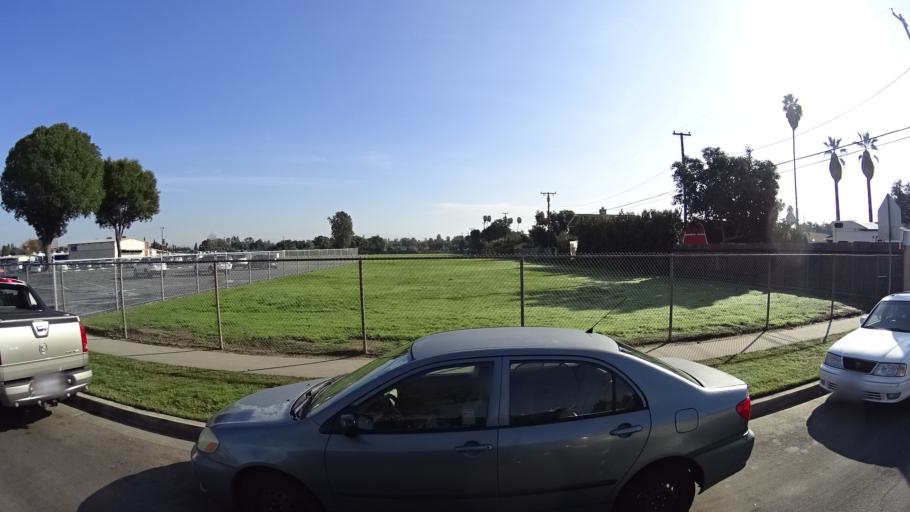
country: US
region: California
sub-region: Orange County
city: Santa Ana
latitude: 33.7699
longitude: -117.8978
